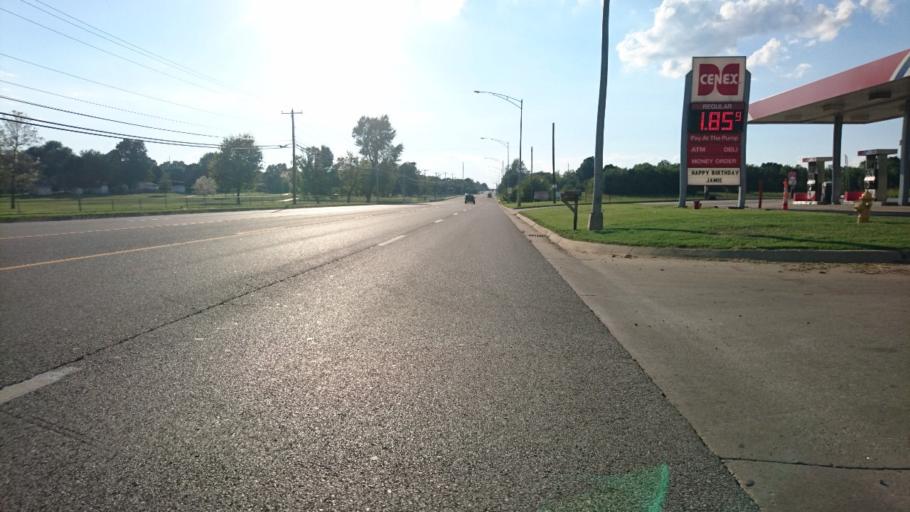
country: US
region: Missouri
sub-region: Greene County
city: Springfield
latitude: 37.2124
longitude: -93.3577
